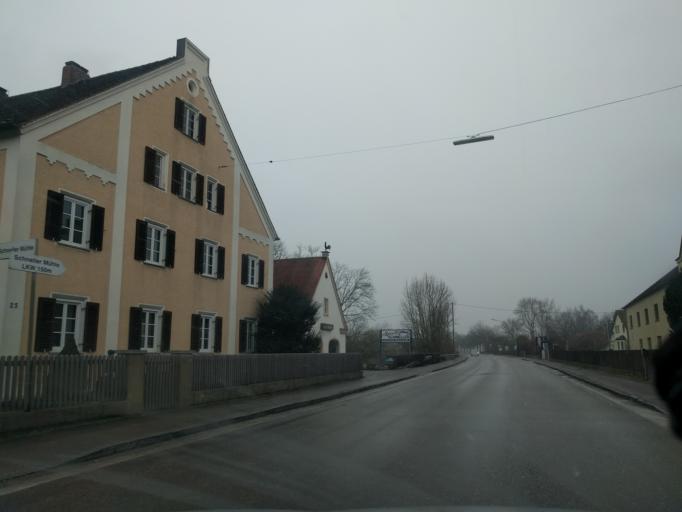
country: DE
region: Bavaria
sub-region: Swabia
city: Donauwoerth
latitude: 48.7038
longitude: 10.7952
